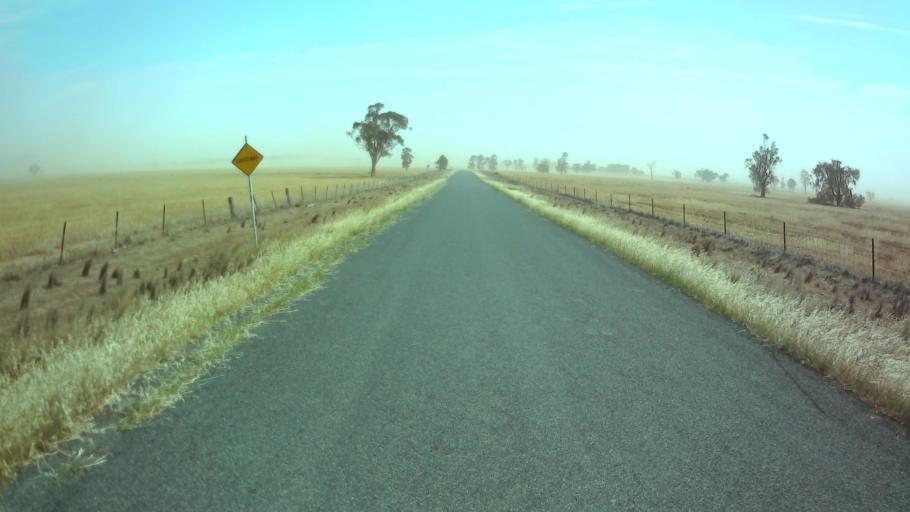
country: AU
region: New South Wales
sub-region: Weddin
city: Grenfell
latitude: -33.7425
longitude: 147.9923
